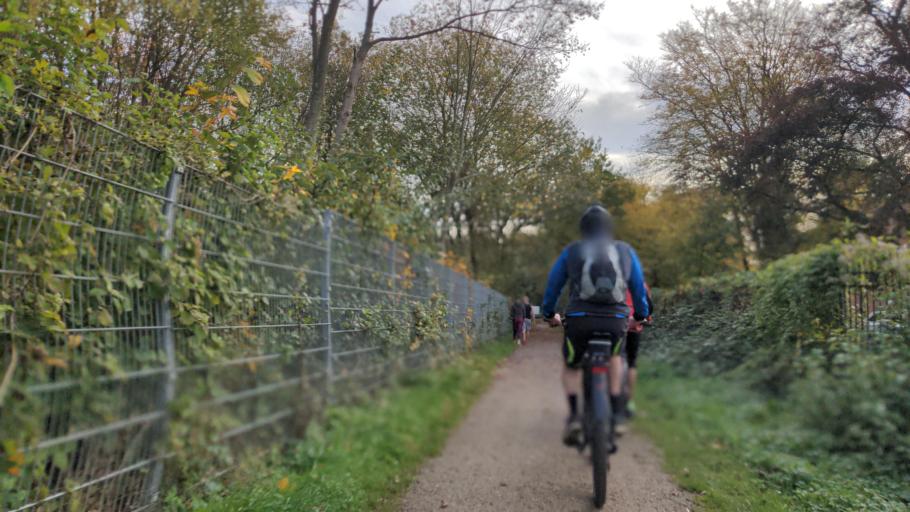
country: DE
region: Schleswig-Holstein
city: Neustadt in Holstein
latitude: 54.1061
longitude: 10.7985
